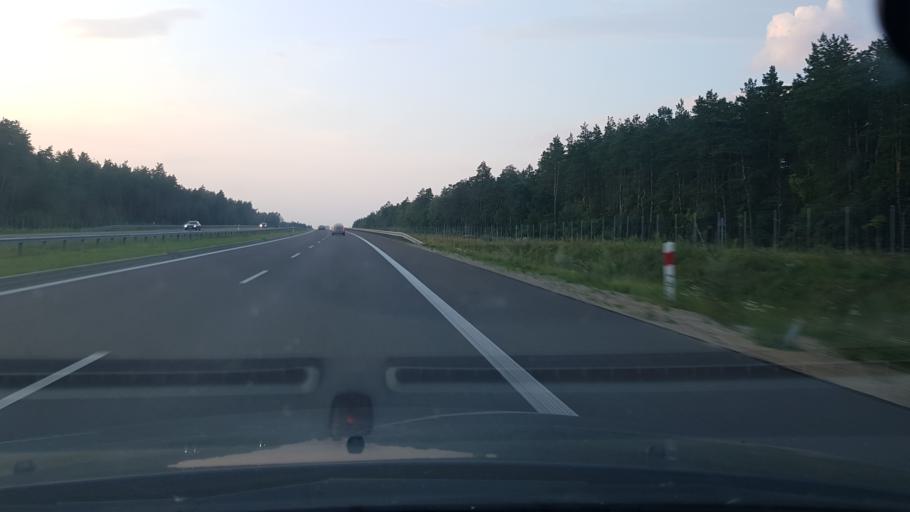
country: PL
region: Masovian Voivodeship
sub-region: Powiat mlawski
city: Wieczfnia Koscielna
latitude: 53.2425
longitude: 20.4243
